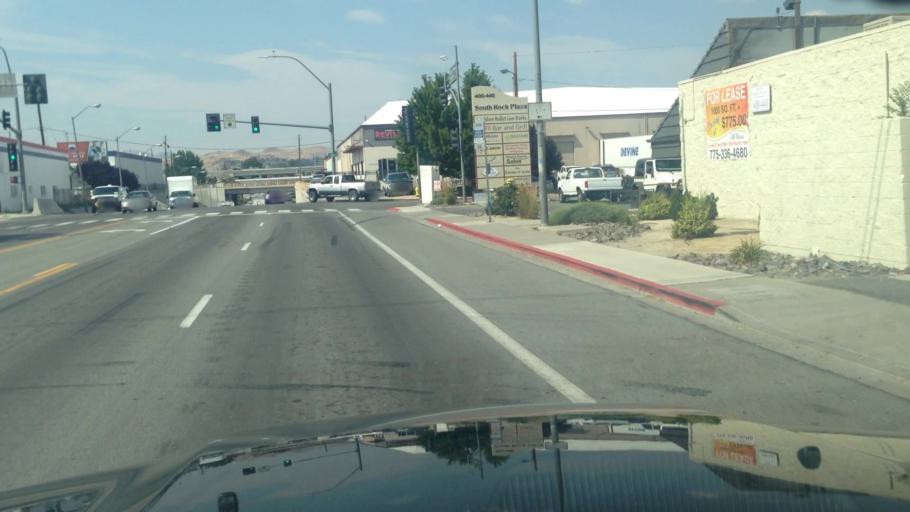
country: US
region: Nevada
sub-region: Washoe County
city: Sparks
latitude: 39.5302
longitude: -119.7662
